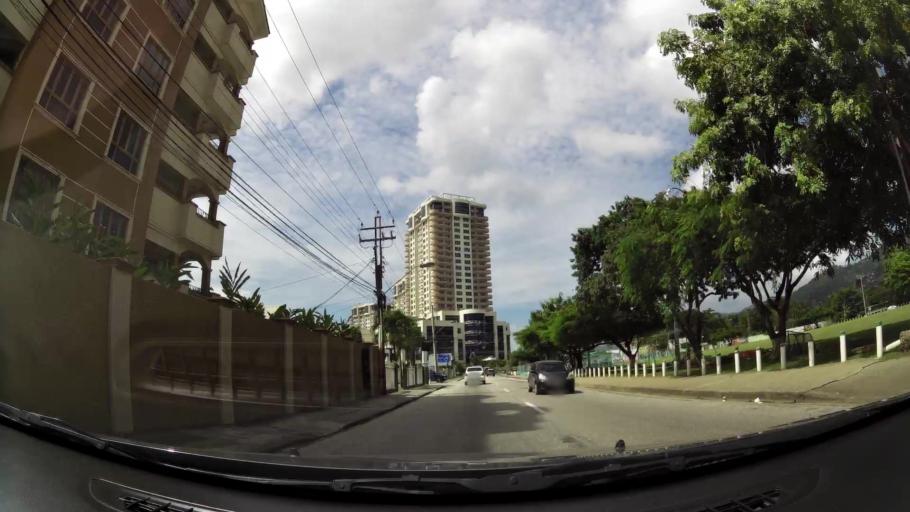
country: TT
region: City of Port of Spain
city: Port-of-Spain
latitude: 10.6683
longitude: -61.5255
